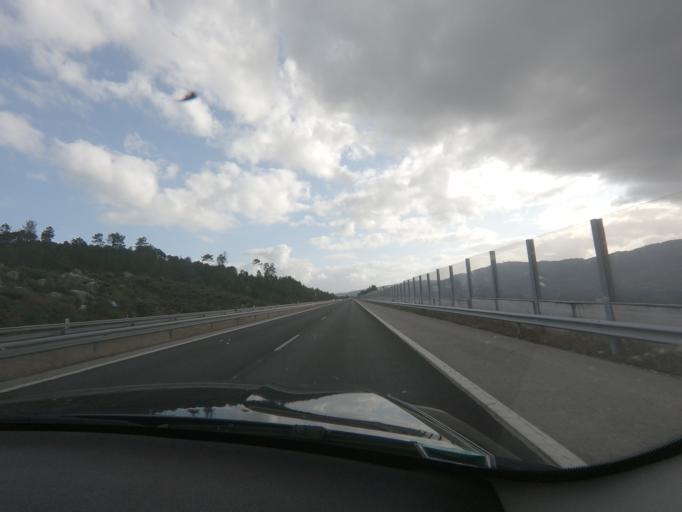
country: PT
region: Viseu
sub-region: Castro Daire
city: Castro Daire
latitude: 40.8744
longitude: -7.9224
